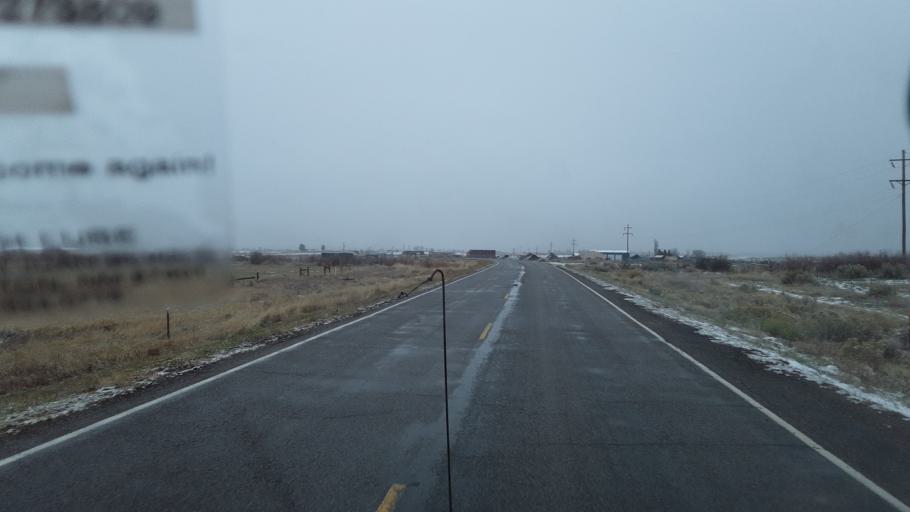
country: US
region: New Mexico
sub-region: Rio Arriba County
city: Tierra Amarilla
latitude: 36.7048
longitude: -106.5582
